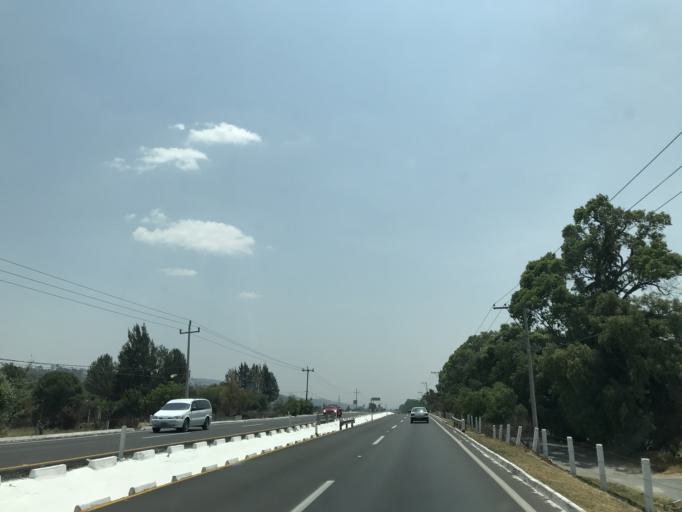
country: MX
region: Tlaxcala
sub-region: Ixtacuixtla de Mariano Matamoros
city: Santa Justina Ecatepec
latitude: 19.3284
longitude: -98.3475
